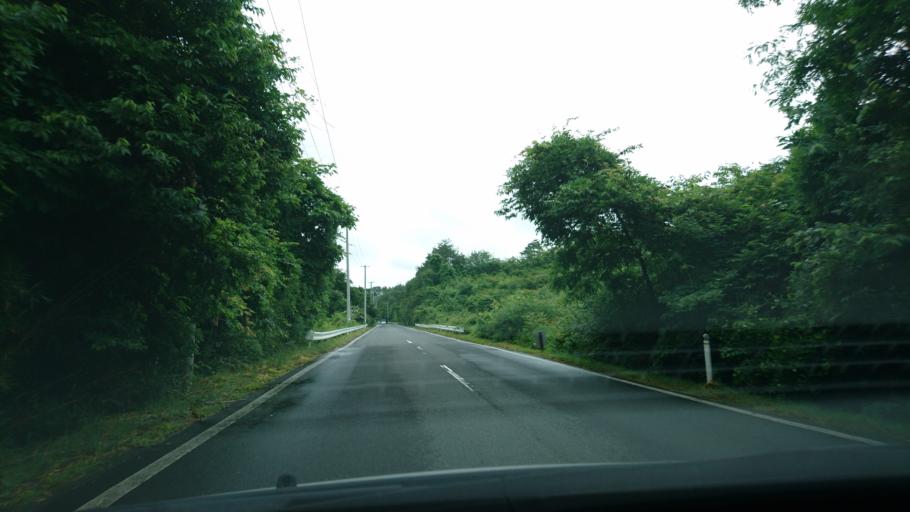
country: JP
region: Iwate
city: Ichinoseki
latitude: 38.8895
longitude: 141.1497
